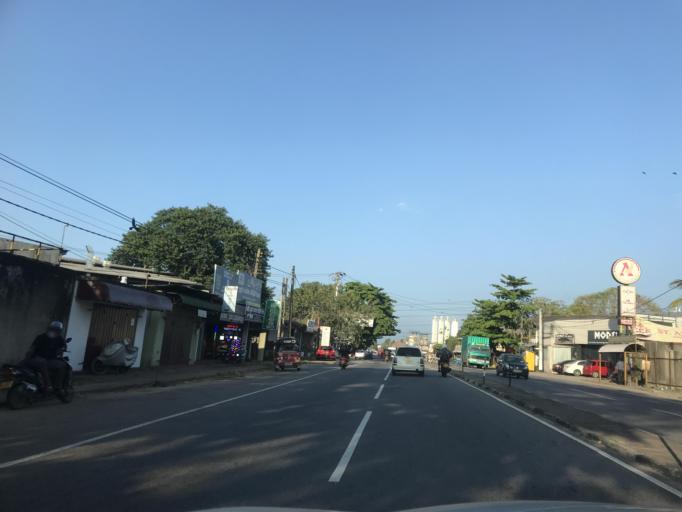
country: LK
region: Western
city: Ja Ela
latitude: 7.0908
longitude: 79.9014
